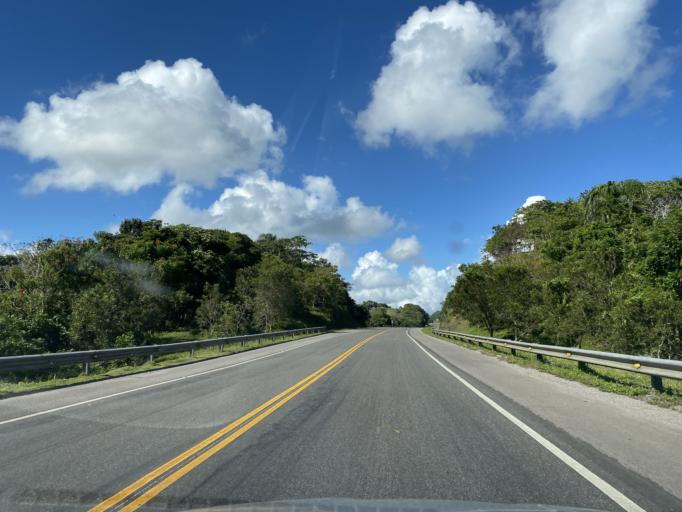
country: DO
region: Monte Plata
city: Majagual
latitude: 19.0312
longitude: -69.8256
